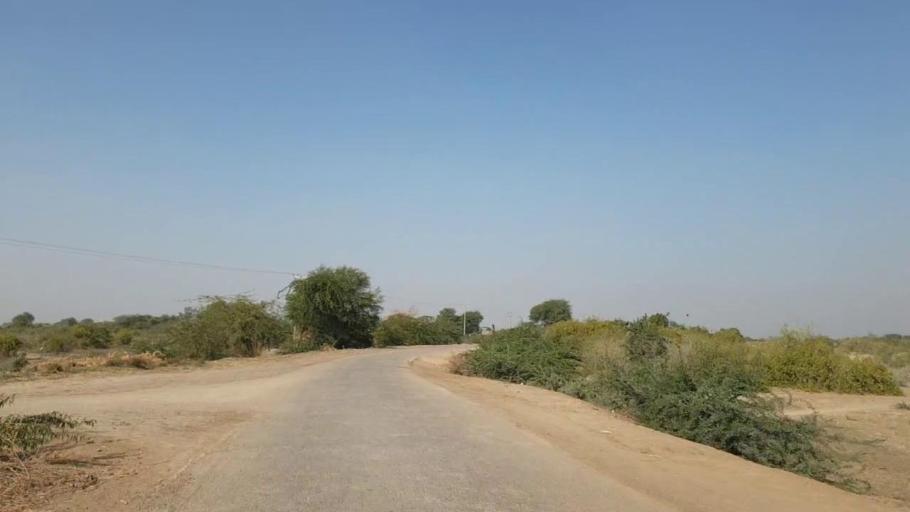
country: PK
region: Sindh
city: Digri
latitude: 24.9974
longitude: 69.1067
